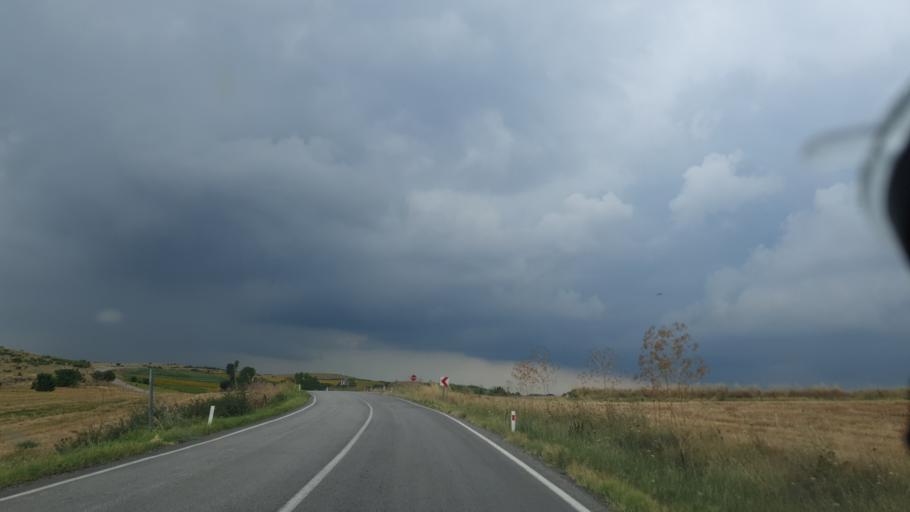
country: TR
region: Tekirdag
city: Hayrabolu
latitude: 41.2279
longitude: 27.0316
